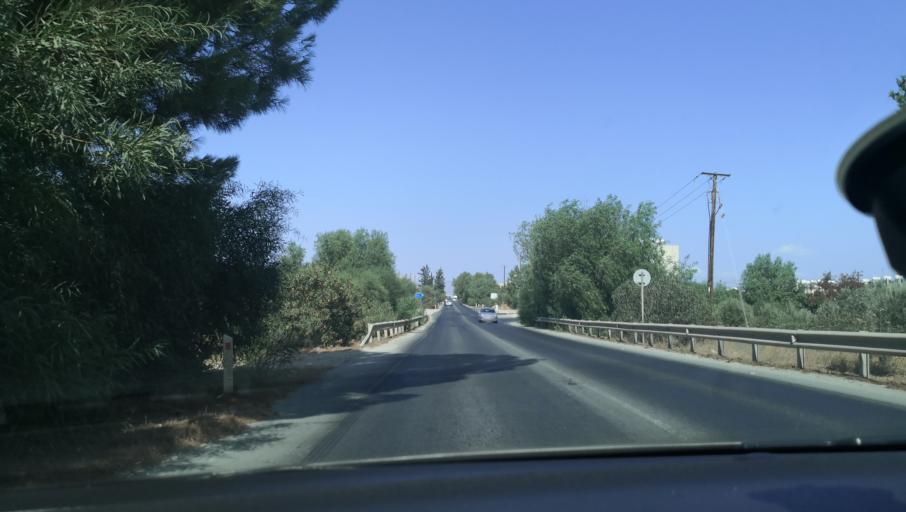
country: CY
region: Lefkosia
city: Kato Deftera
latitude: 35.1003
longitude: 33.2870
